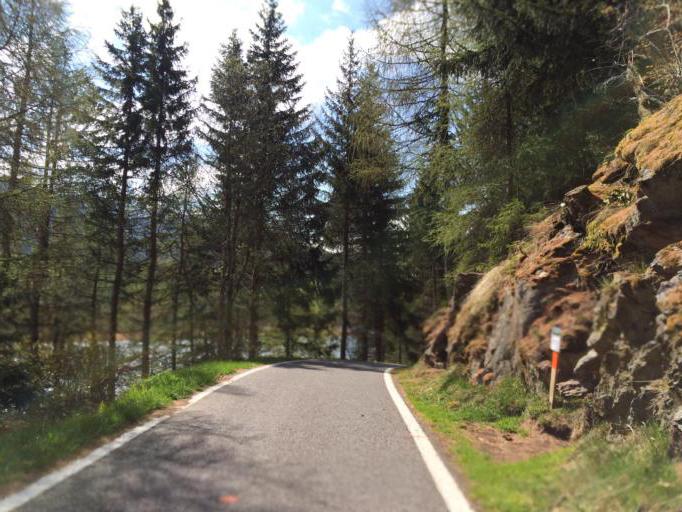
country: IT
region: Trentino-Alto Adige
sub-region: Bolzano
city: Malles Venosta
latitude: 46.7473
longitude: 10.5282
